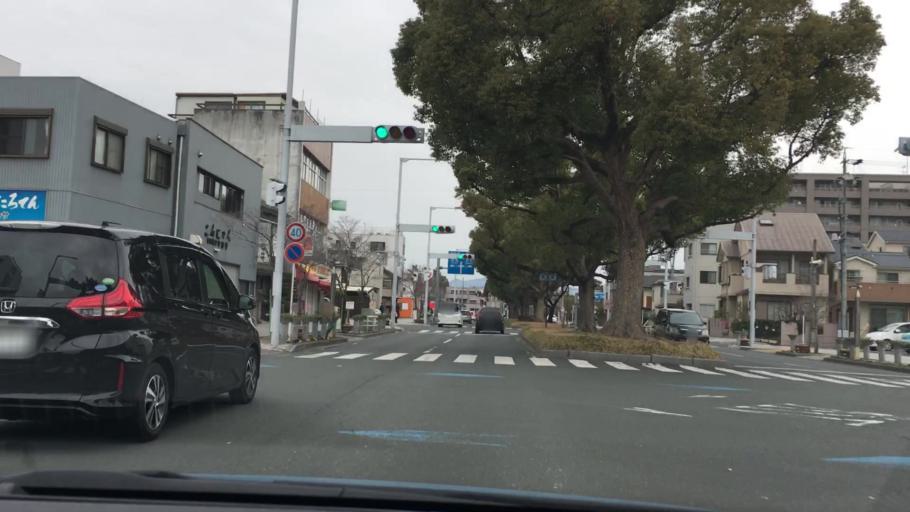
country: JP
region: Aichi
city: Toyohashi
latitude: 34.7651
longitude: 137.3949
